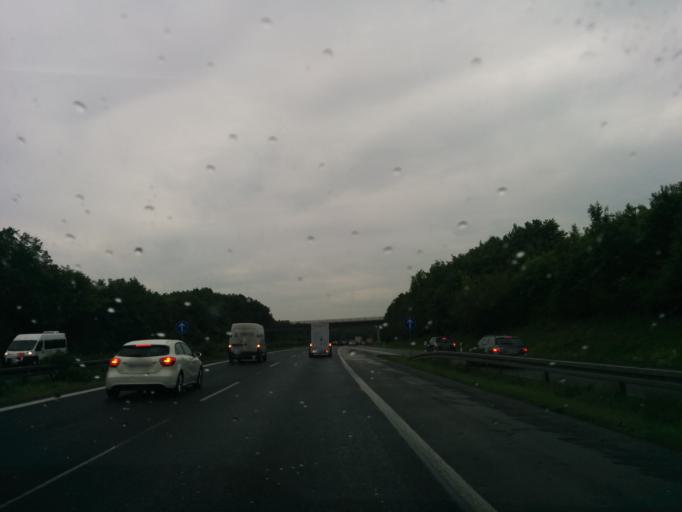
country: DE
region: Bavaria
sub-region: Regierungsbezirk Unterfranken
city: Estenfeld
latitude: 49.8494
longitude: 10.0047
